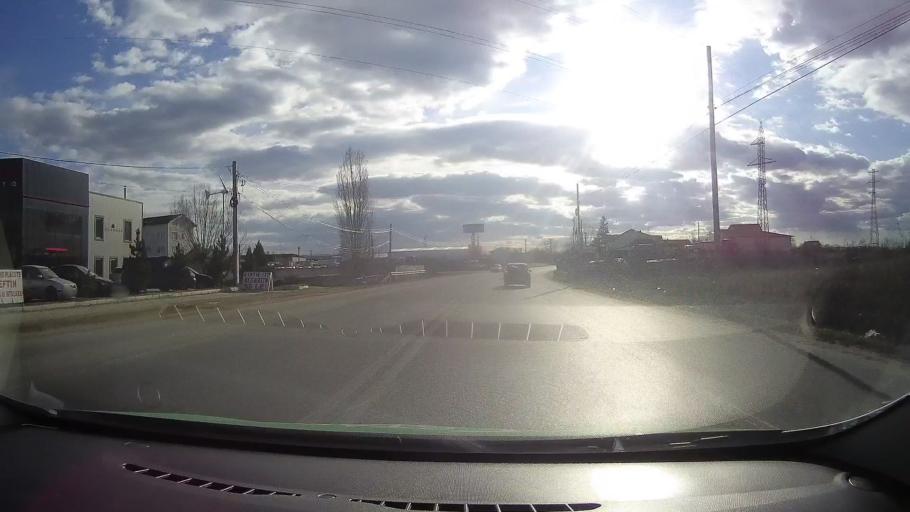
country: RO
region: Dambovita
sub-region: Comuna Lucieni
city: Lucieni
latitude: 44.8470
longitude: 25.4448
